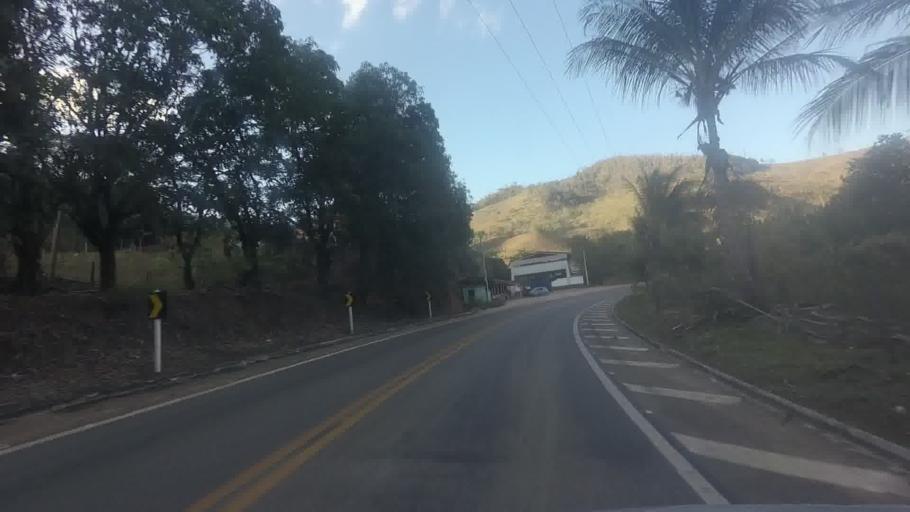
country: BR
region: Espirito Santo
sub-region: Cachoeiro De Itapemirim
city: Cachoeiro de Itapemirim
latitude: -20.8229
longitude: -41.2047
